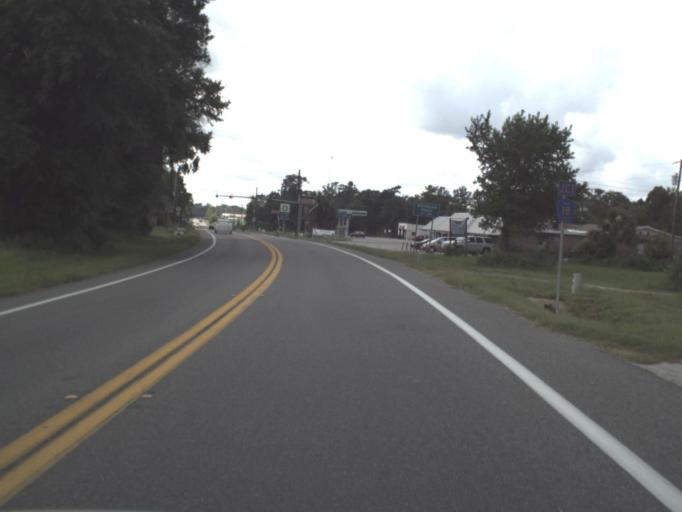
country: US
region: Florida
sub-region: Union County
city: Lake Butler
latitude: 29.9479
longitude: -82.4249
